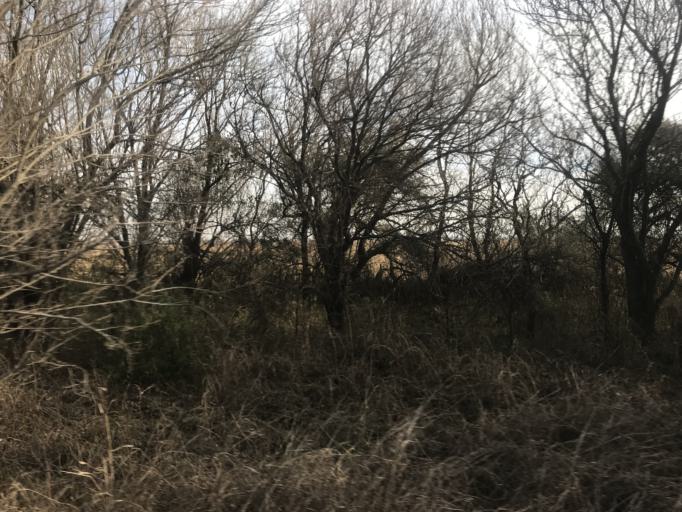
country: AR
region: Cordoba
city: Pilar
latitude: -31.7204
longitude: -63.8523
